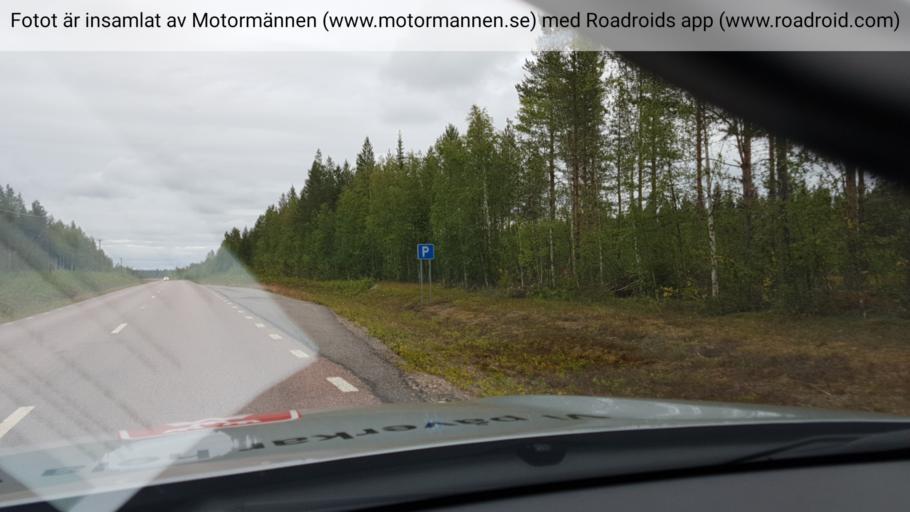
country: SE
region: Norrbotten
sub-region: Pajala Kommun
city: Pajala
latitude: 67.0962
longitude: 22.5774
